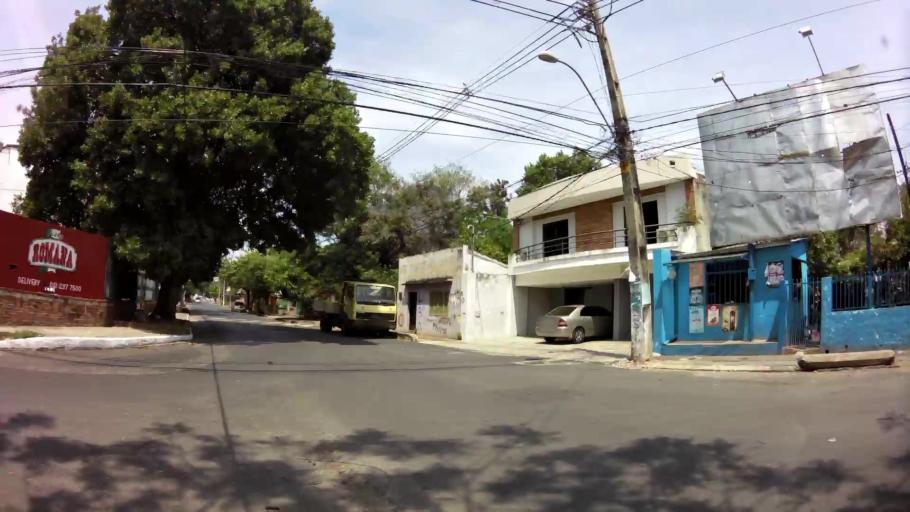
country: PY
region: Asuncion
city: Asuncion
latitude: -25.2839
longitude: -57.5907
